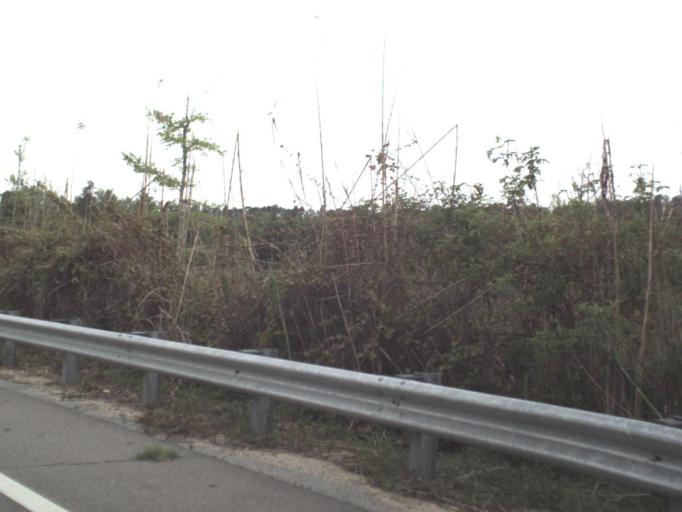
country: US
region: Florida
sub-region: Escambia County
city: East Pensacola Heights
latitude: 30.4795
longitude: -87.1633
